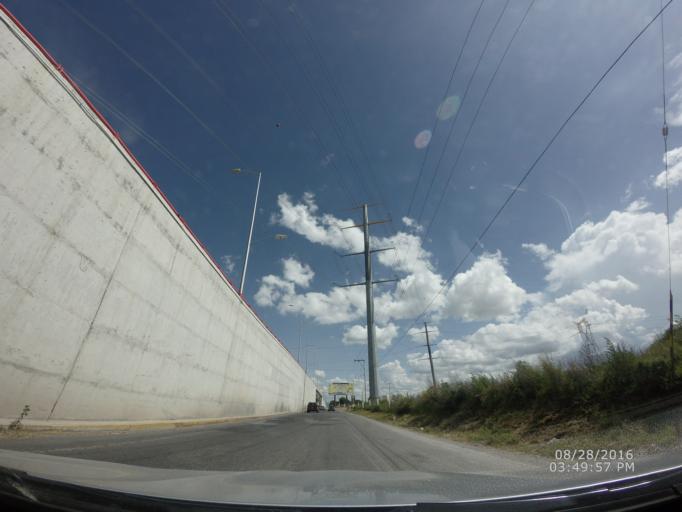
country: MX
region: Hidalgo
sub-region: Mineral de la Reforma
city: Rinconada de los Angeles
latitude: 20.0386
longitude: -98.7324
